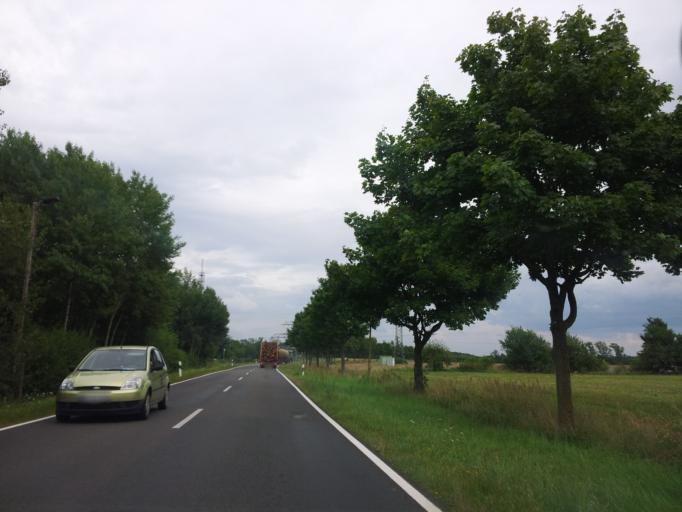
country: DE
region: Brandenburg
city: Belzig
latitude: 52.1555
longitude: 12.5359
